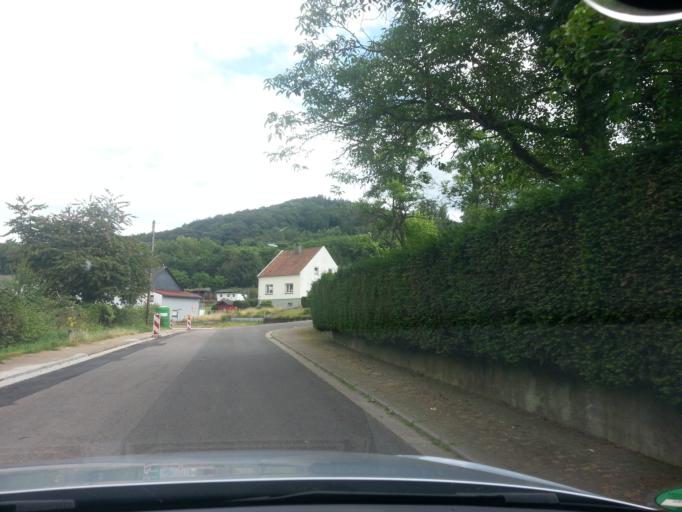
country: DE
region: Saarland
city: Nalbach
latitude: 49.4128
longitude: 6.7711
